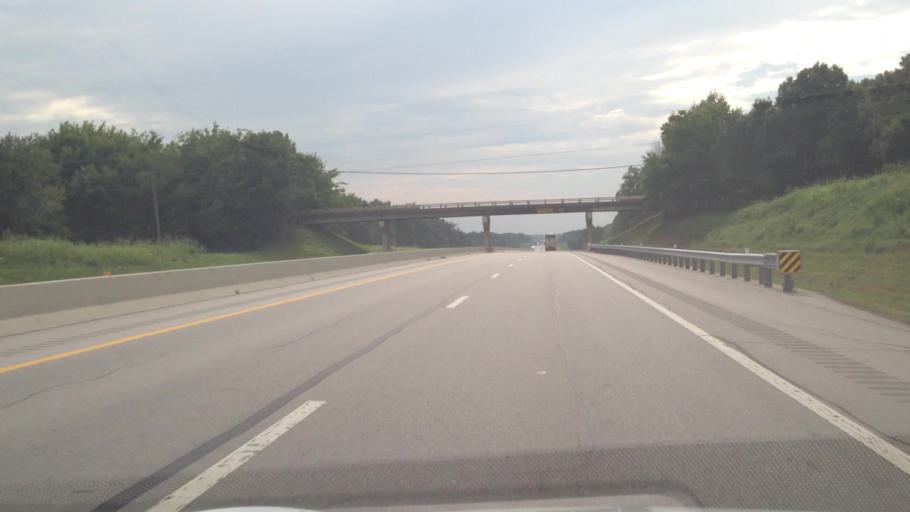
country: US
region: Kansas
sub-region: Cherokee County
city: Baxter Springs
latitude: 36.9347
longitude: -94.7110
